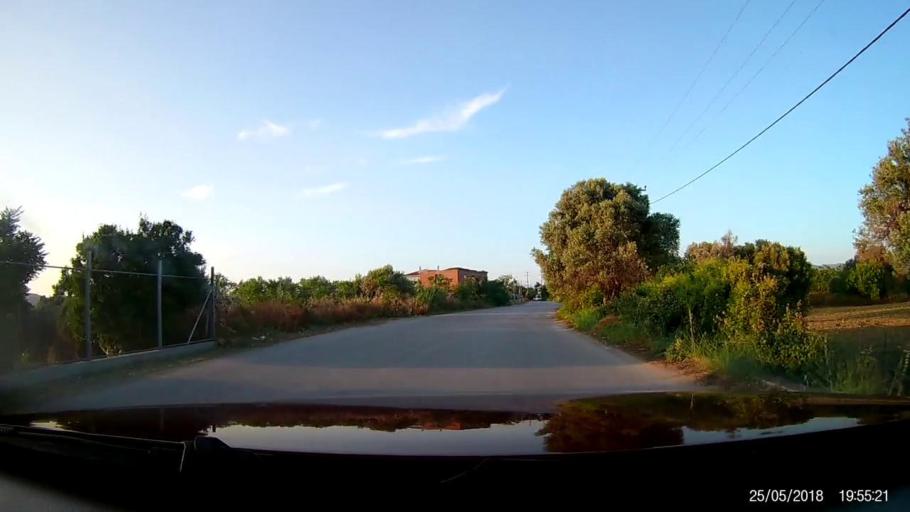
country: GR
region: Central Greece
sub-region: Nomos Evvoias
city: Ayios Nikolaos
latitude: 38.4244
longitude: 23.6579
